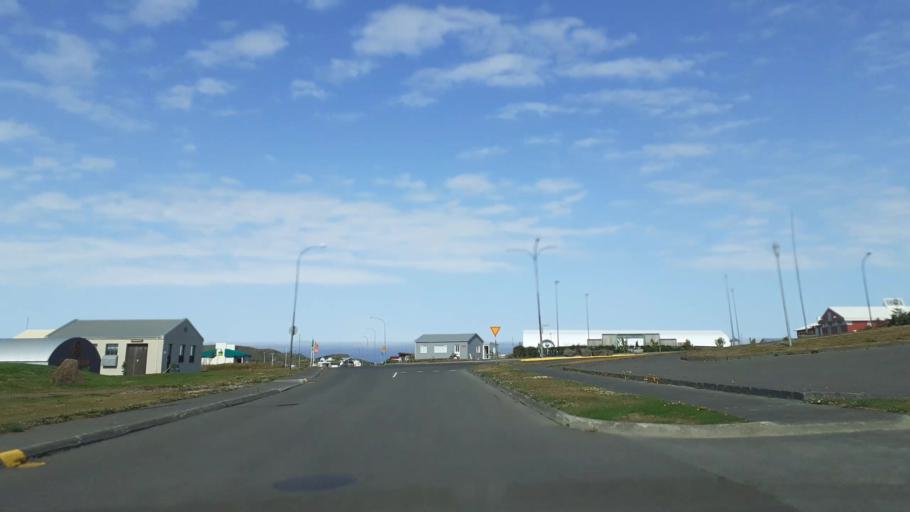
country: IS
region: Northwest
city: Saudarkrokur
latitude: 65.8225
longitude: -20.3040
